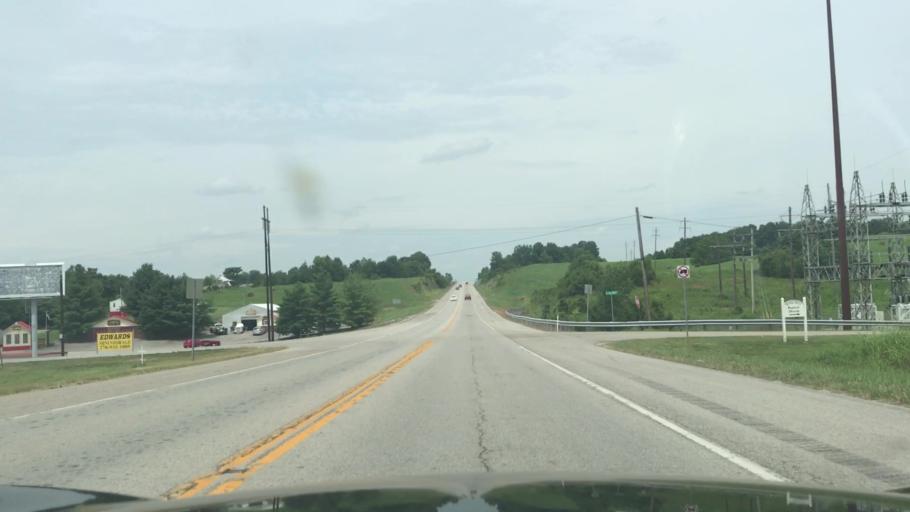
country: US
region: Kentucky
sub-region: Green County
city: Greensburg
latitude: 37.2761
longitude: -85.5105
